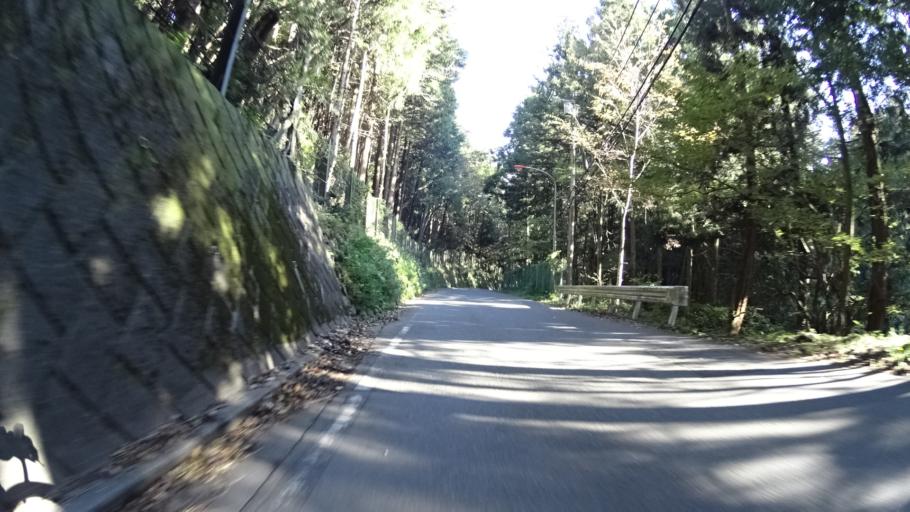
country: JP
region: Yamanashi
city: Uenohara
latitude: 35.6402
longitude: 139.1343
